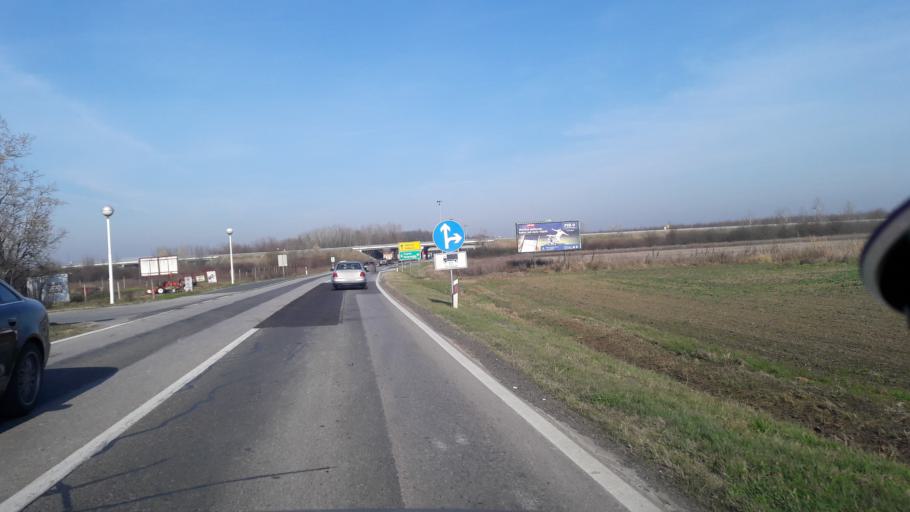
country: HR
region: Vukovarsko-Srijemska
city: Zupanja
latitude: 45.1027
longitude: 18.7008
